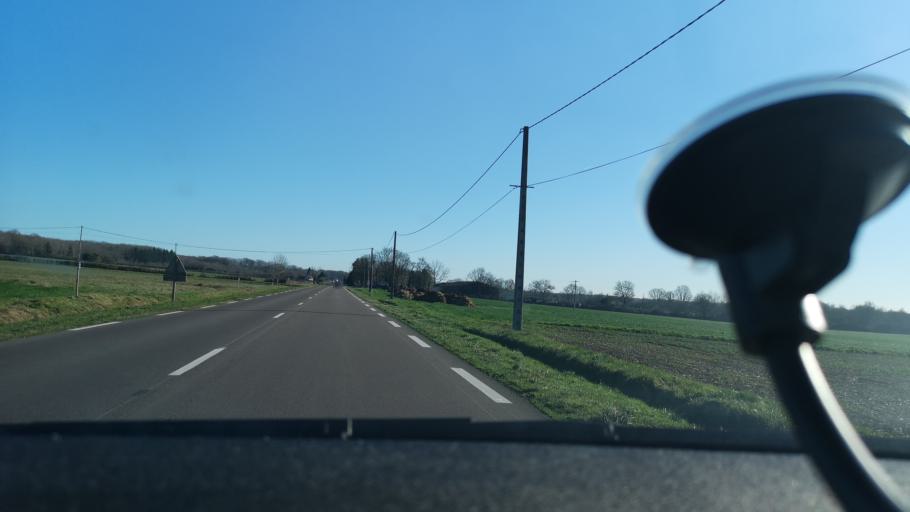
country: FR
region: Bourgogne
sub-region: Departement de Saone-et-Loire
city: Ouroux-sur-Saone
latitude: 46.7736
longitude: 4.9654
